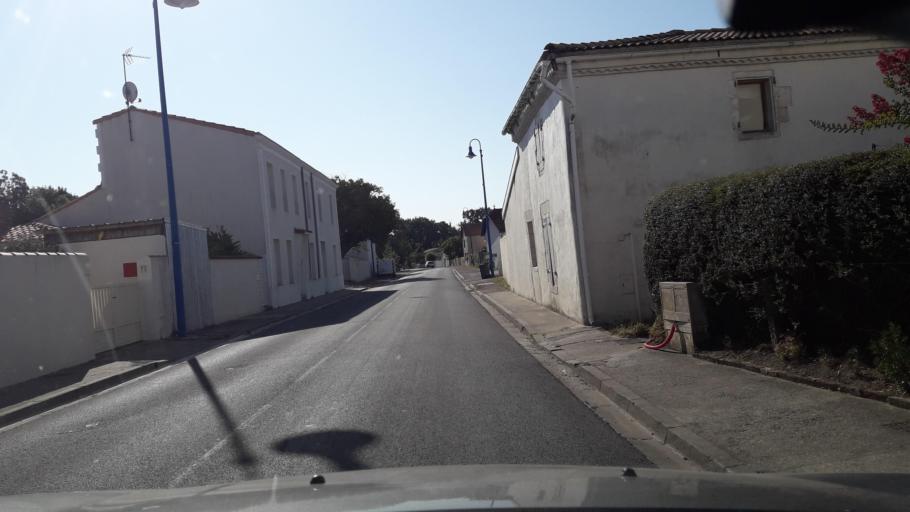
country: FR
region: Poitou-Charentes
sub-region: Departement de la Charente-Maritime
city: Etaules
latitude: 45.7310
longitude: -1.0967
